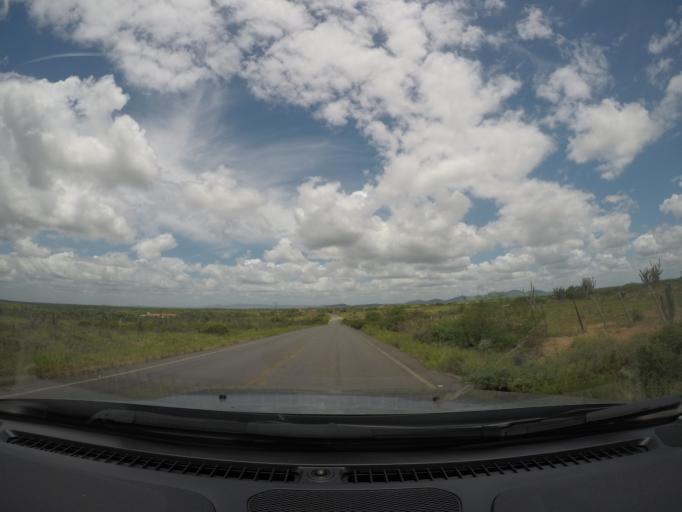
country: BR
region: Bahia
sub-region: Ipira
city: Ipira
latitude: -12.3059
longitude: -39.9016
